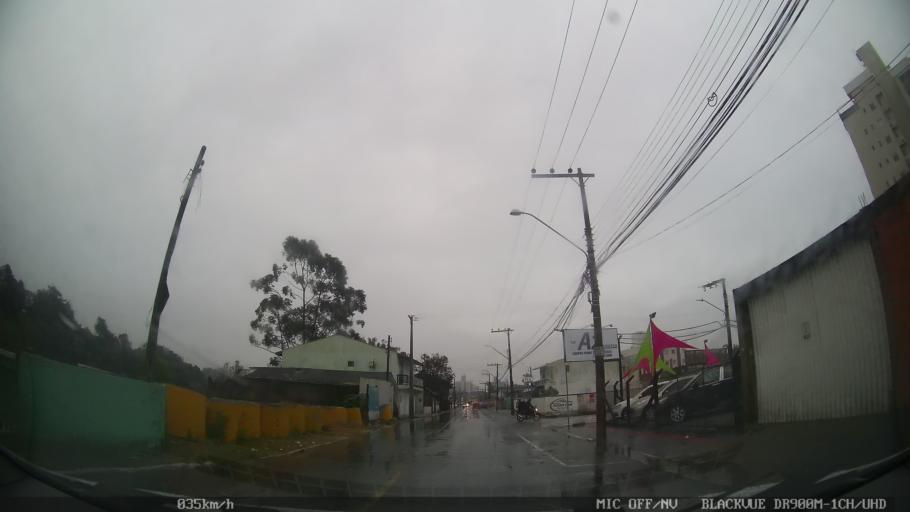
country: BR
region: Santa Catarina
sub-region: Itajai
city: Itajai
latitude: -26.9156
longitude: -48.6830
